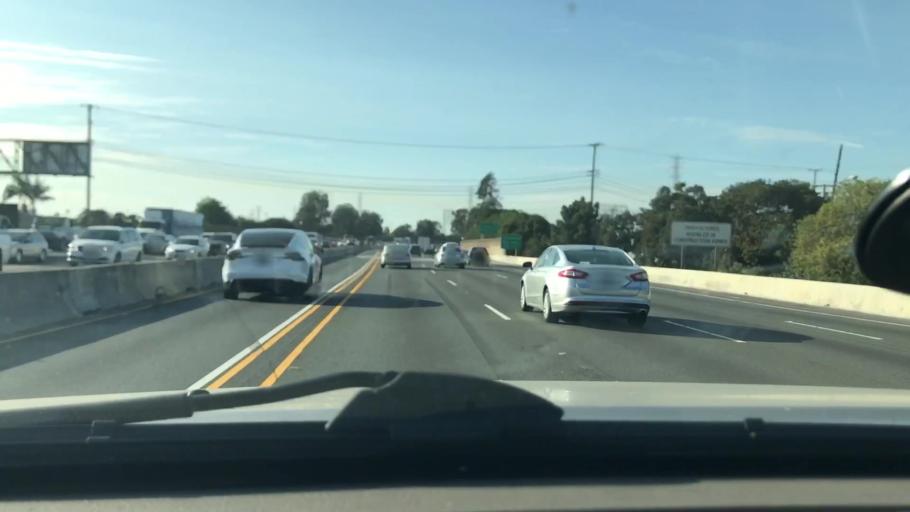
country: US
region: California
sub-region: Los Angeles County
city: Alondra Park
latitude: 33.8669
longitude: -118.3340
